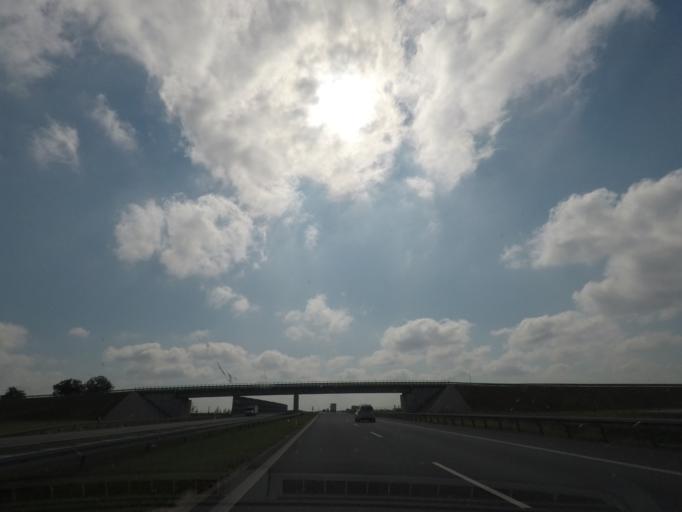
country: PL
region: Kujawsko-Pomorskie
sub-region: Powiat wloclawski
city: Brzesc Kujawski
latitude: 52.6636
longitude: 18.9137
